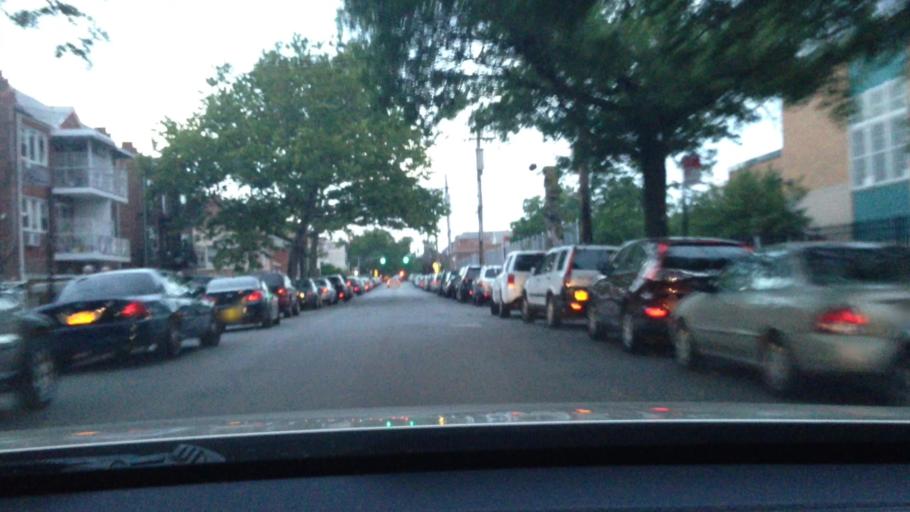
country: US
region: New York
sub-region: Kings County
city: East New York
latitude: 40.6333
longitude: -73.9082
